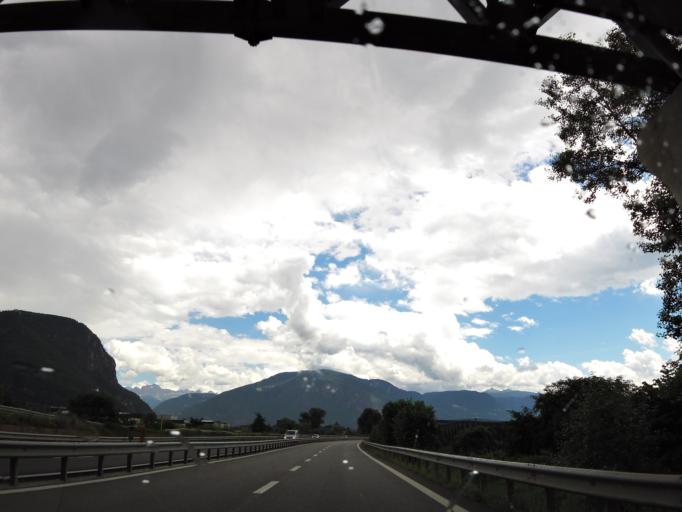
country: IT
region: Trentino-Alto Adige
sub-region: Bolzano
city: Terlano
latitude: 46.5112
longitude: 11.2598
